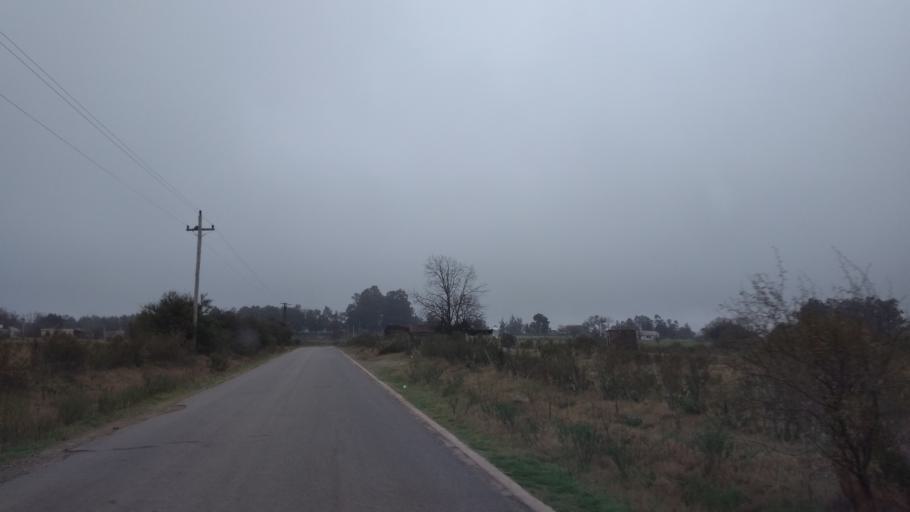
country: UY
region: Florida
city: Florida
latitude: -34.0834
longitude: -56.2053
